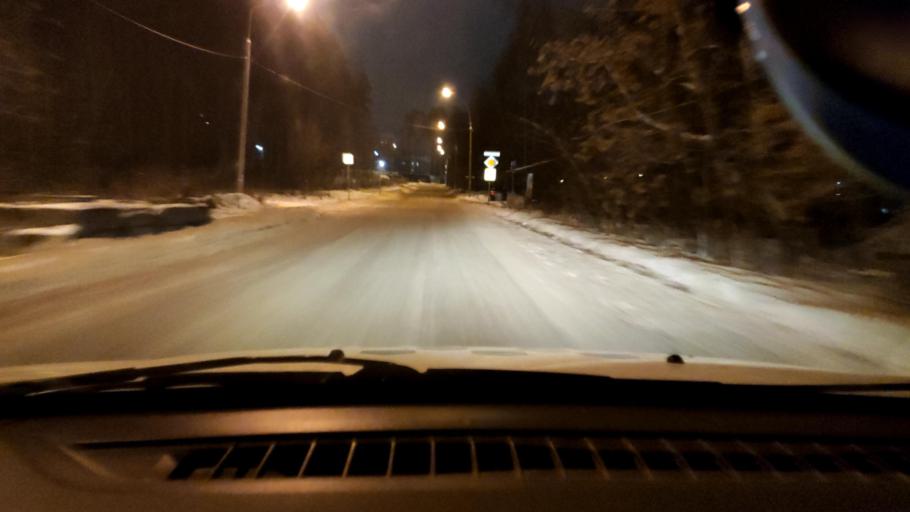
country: RU
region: Perm
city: Kondratovo
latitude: 58.0293
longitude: 56.0114
